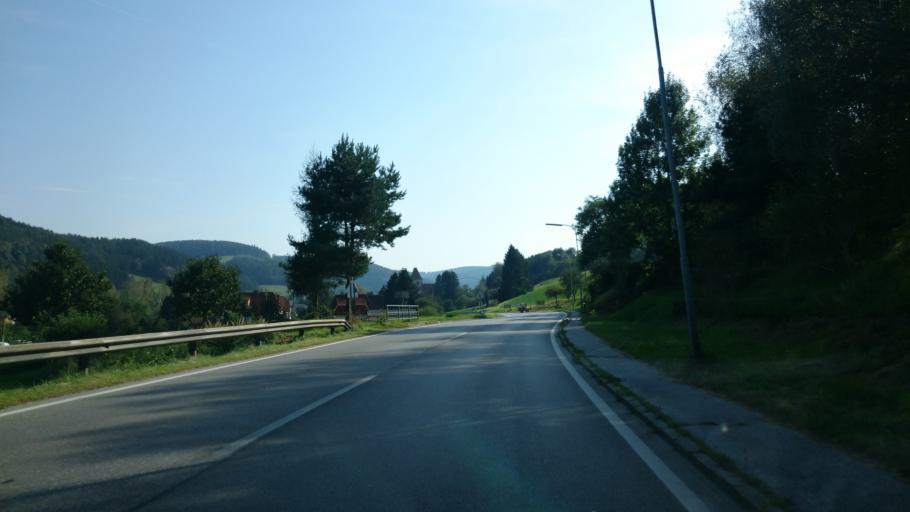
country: AT
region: Lower Austria
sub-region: Politischer Bezirk Neunkirchen
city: Edlitz
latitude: 47.5752
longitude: 16.0996
